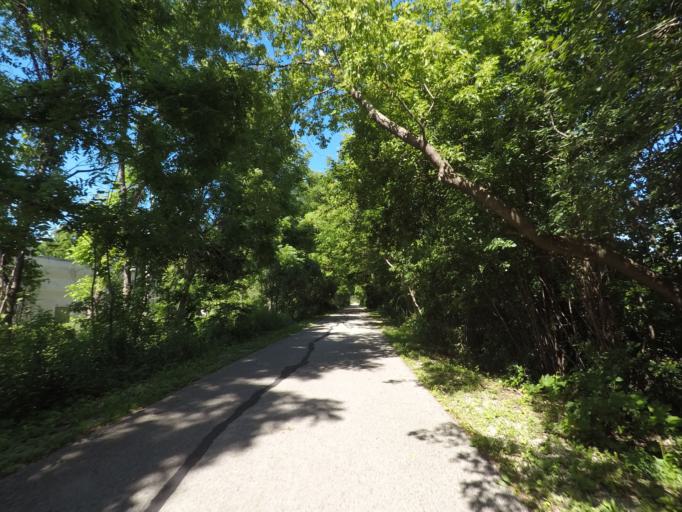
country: US
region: Wisconsin
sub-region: Milwaukee County
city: West Allis
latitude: 43.0251
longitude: -88.0254
